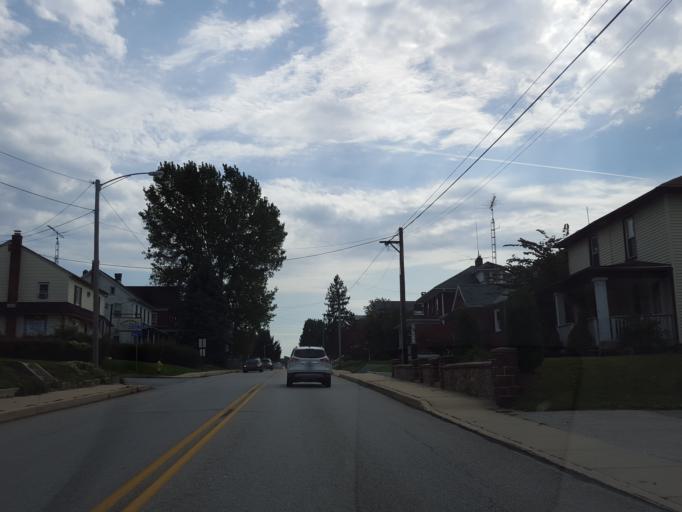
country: US
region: Pennsylvania
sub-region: York County
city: Spry
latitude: 39.9197
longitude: -76.6854
